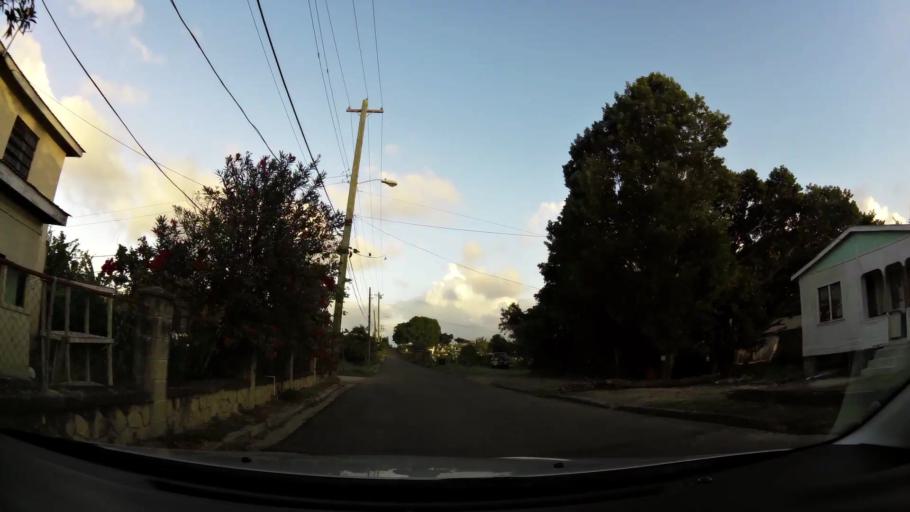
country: AG
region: Saint John
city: Saint John's
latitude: 17.1301
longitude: -61.8395
